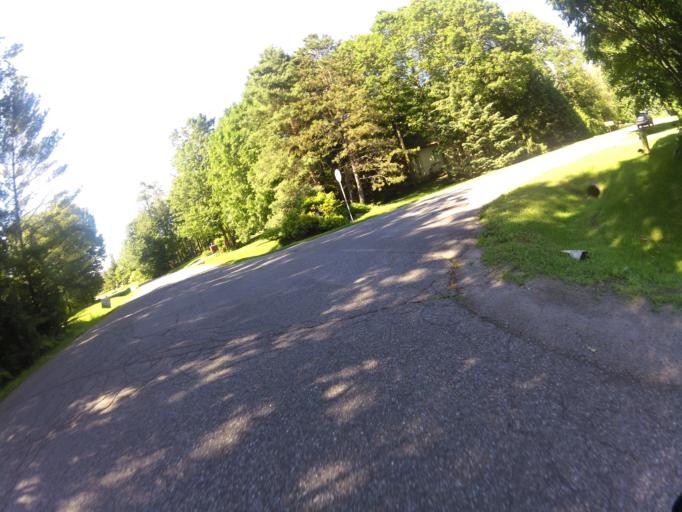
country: CA
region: Ontario
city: Bells Corners
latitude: 45.2804
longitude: -75.7844
